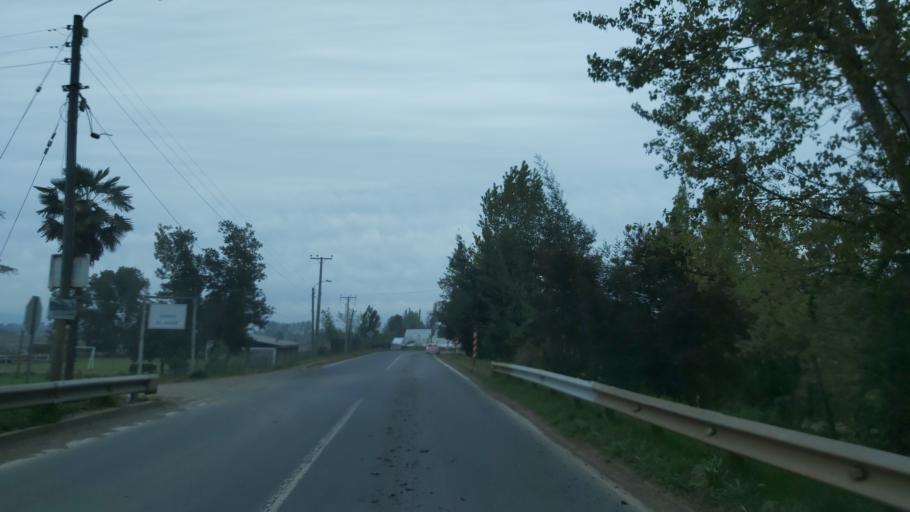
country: CL
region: Maule
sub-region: Provincia de Linares
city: Colbun
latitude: -35.7519
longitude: -71.4951
